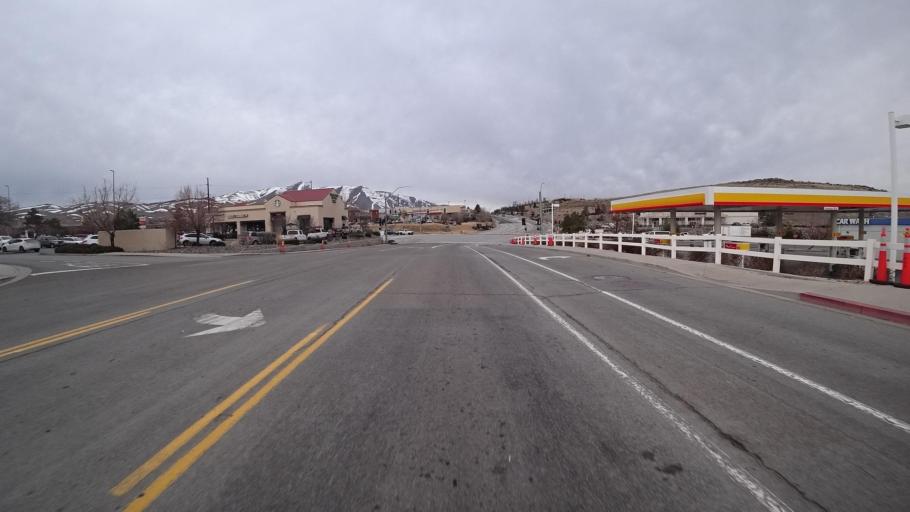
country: US
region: Nevada
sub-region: Washoe County
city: Golden Valley
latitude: 39.6140
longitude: -119.8479
